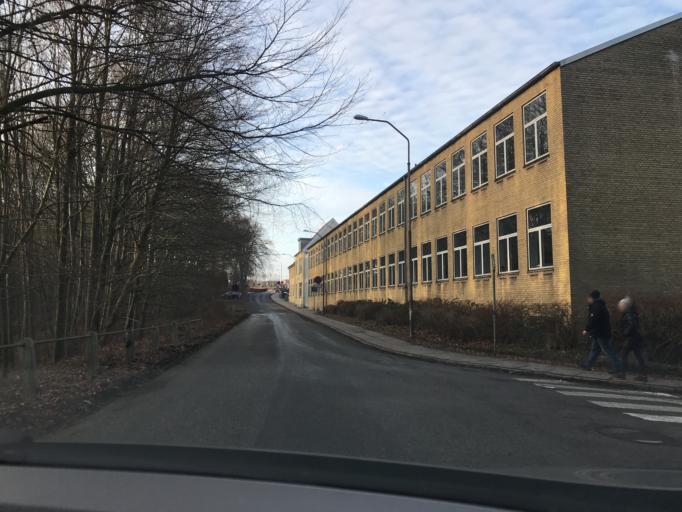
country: DK
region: South Denmark
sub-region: Vejle Kommune
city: Vejle
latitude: 55.6913
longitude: 9.5305
